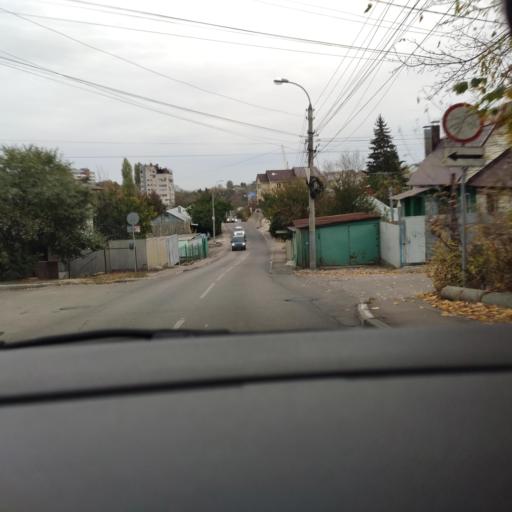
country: RU
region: Voronezj
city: Voronezh
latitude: 51.6566
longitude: 39.1974
